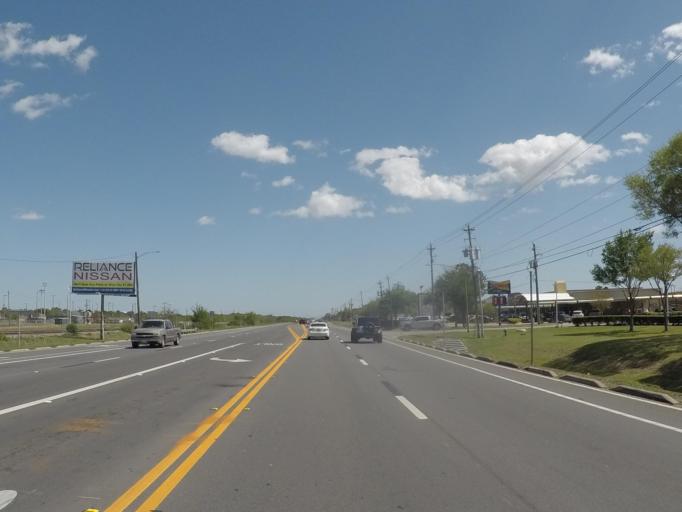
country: US
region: Texas
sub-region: Harris County
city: Webster
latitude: 29.5799
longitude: -95.1576
